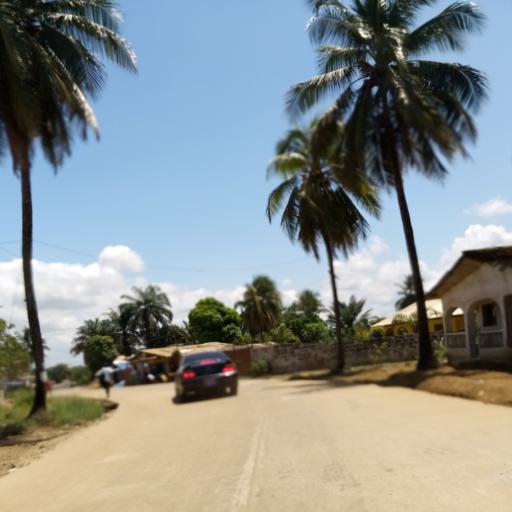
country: LR
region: Montserrado
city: Monrovia
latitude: 6.2439
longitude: -10.6928
